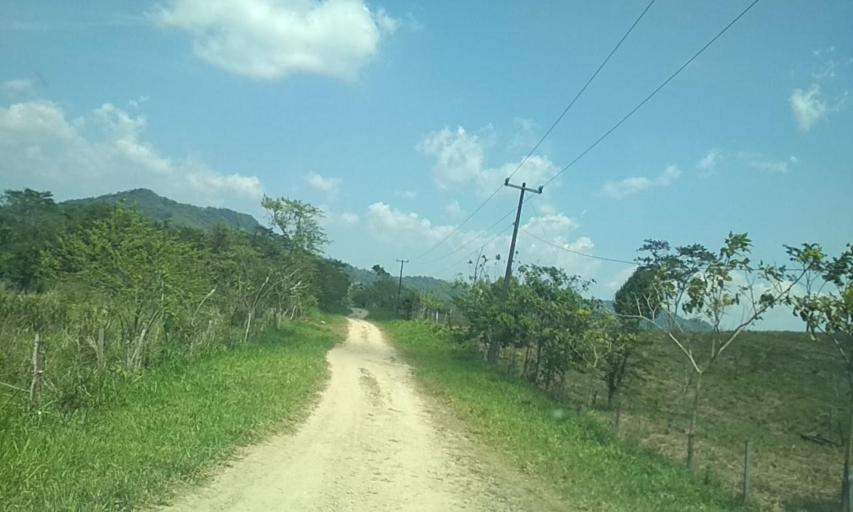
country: MX
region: Chiapas
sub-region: Tecpatan
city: Raudales Malpaso
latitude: 17.3006
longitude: -93.8197
